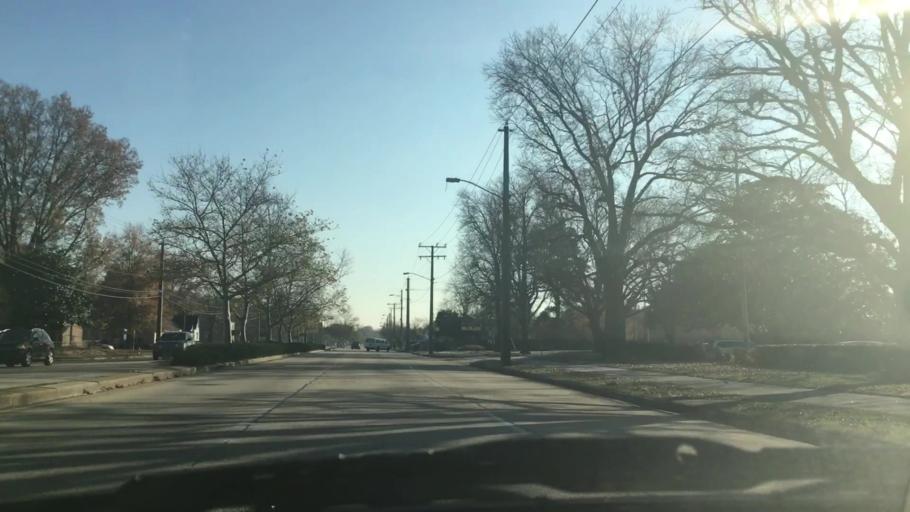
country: US
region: Virginia
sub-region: City of Norfolk
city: Norfolk
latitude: 36.8979
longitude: -76.2389
